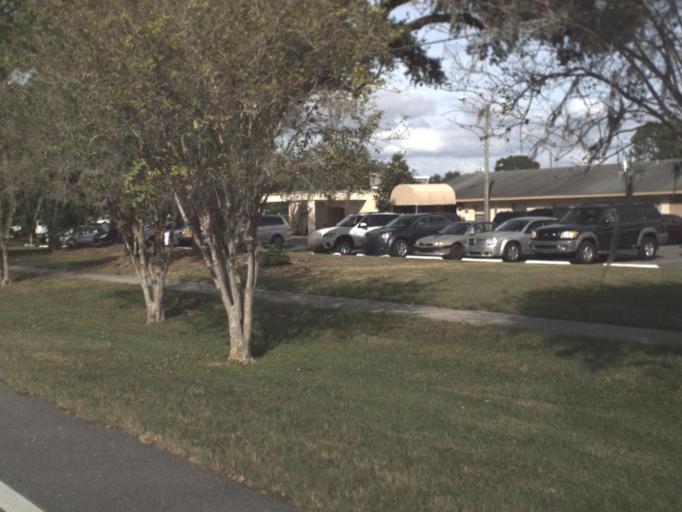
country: US
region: Florida
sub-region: Osceola County
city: Kissimmee
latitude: 28.3180
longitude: -81.4159
